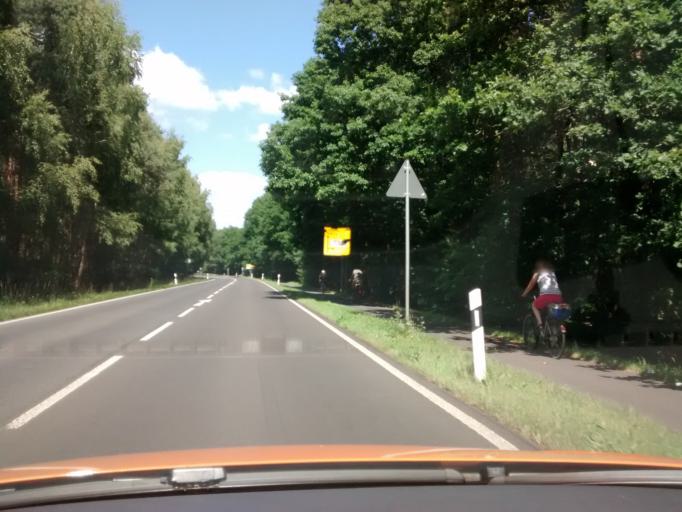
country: DE
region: Berlin
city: Kladow
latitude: 52.4938
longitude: 13.1219
